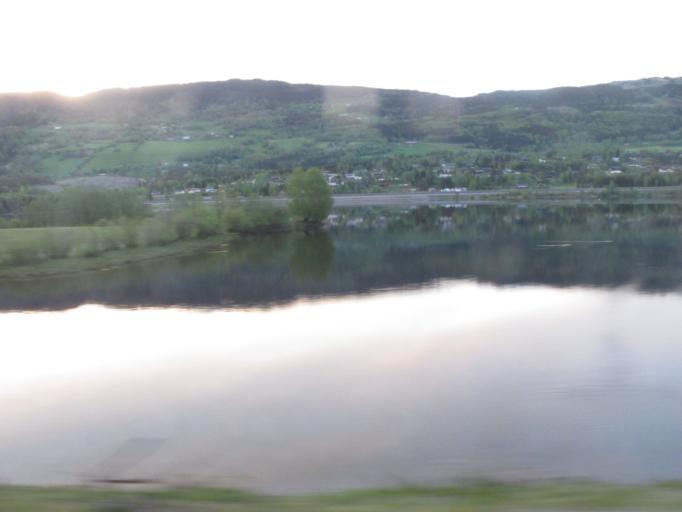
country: NO
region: Oppland
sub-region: Lillehammer
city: Lillehammer
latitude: 61.2480
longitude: 10.4248
